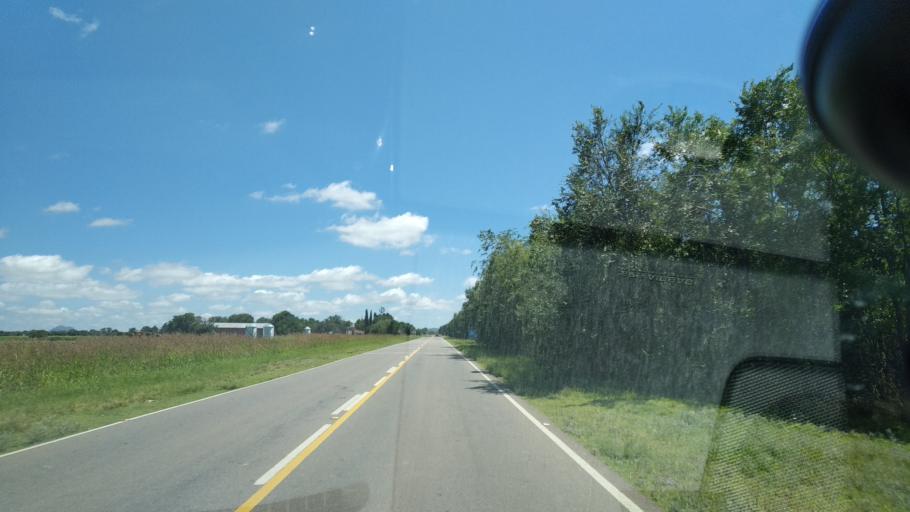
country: AR
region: Cordoba
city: Salsacate
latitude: -31.5017
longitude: -65.1101
